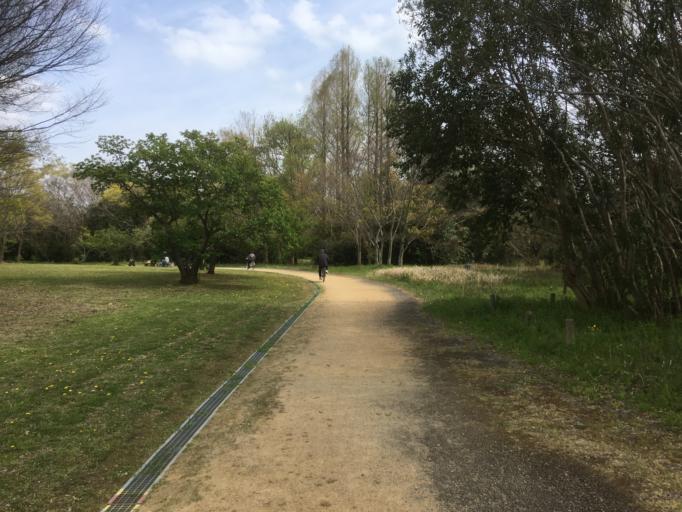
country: JP
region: Nara
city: Tawaramoto
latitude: 34.5964
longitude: 135.7811
